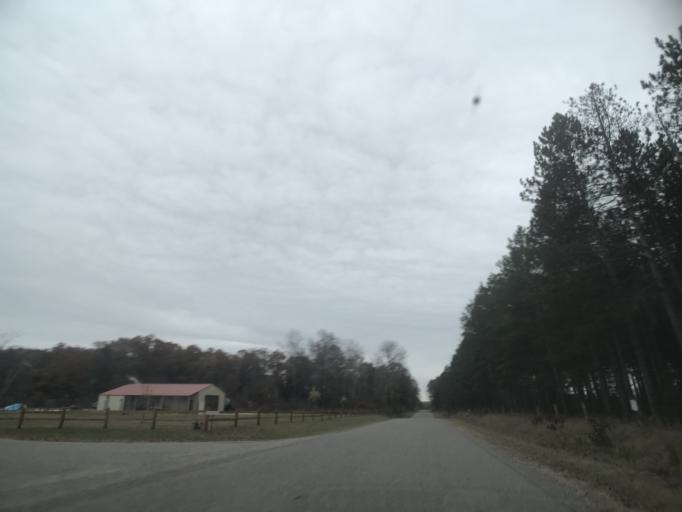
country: US
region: Wisconsin
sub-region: Oconto County
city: Gillett
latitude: 45.3439
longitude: -88.2860
